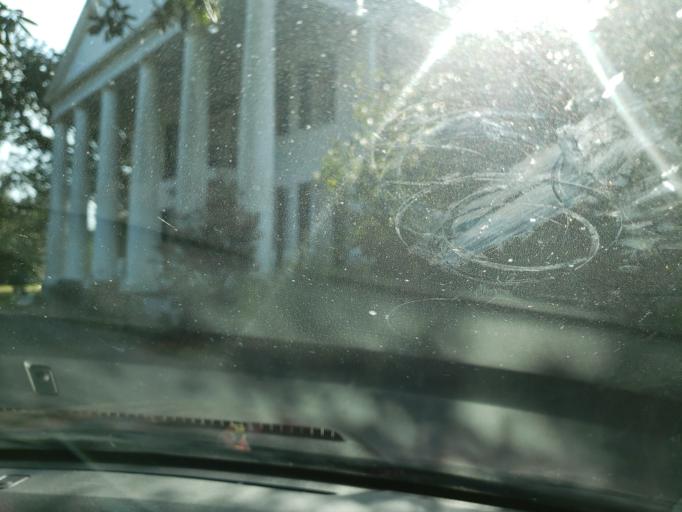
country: US
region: Alabama
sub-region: Hale County
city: Greensboro
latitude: 32.7044
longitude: -87.6078
